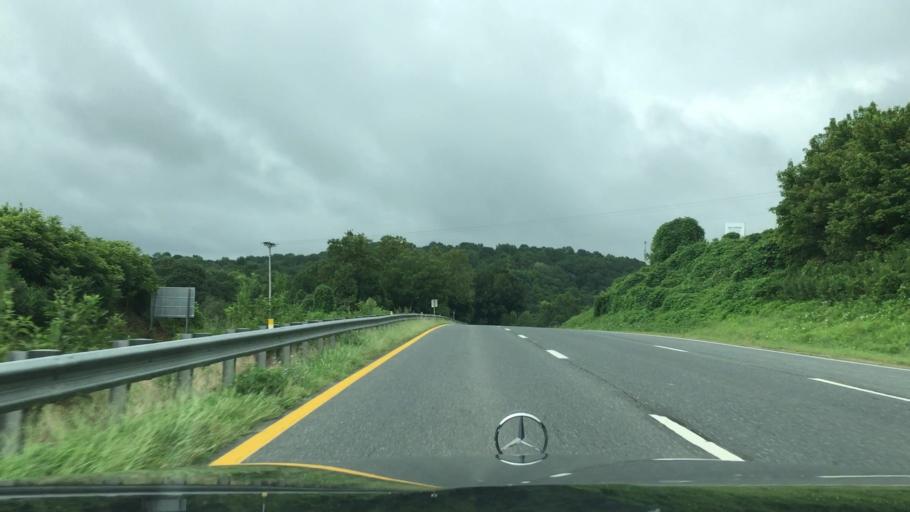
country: US
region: Virginia
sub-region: Amherst County
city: Madison Heights
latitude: 37.3862
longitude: -79.0601
